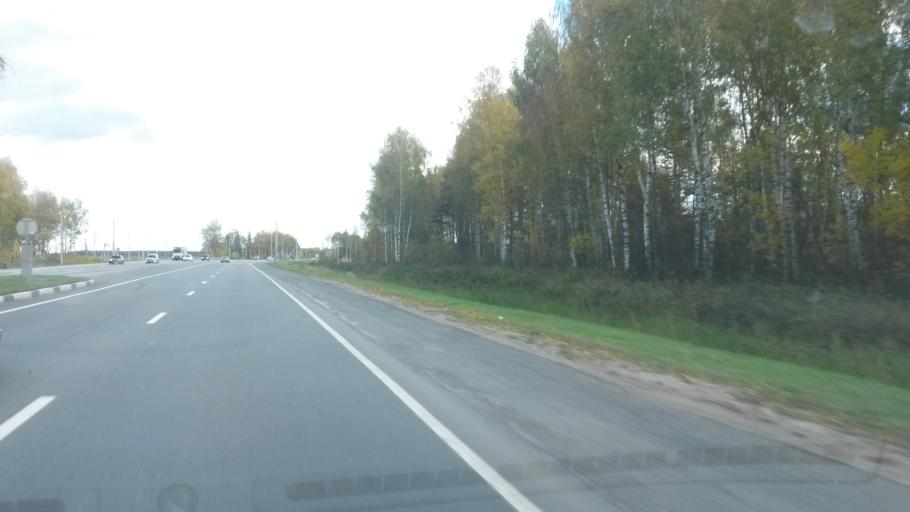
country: RU
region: Jaroslavl
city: Tunoshna
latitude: 57.5400
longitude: 39.9942
